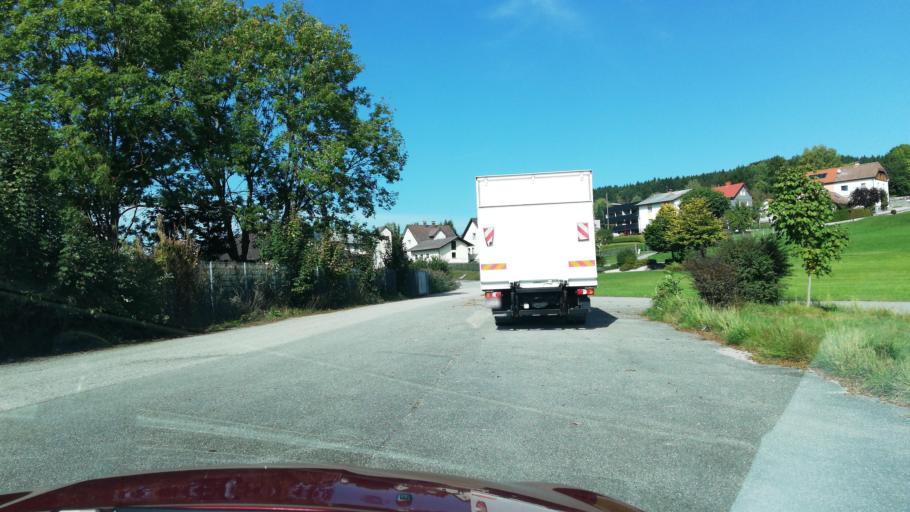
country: AT
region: Upper Austria
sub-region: Politischer Bezirk Vocklabruck
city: Redleiten
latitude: 48.0911
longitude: 13.5622
